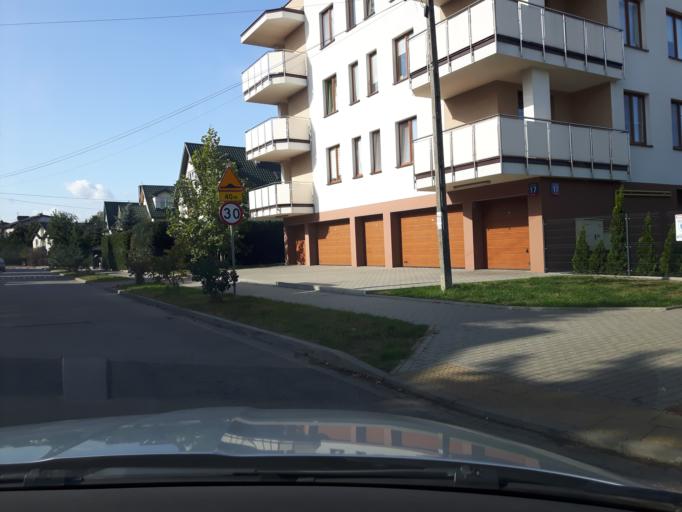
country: PL
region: Masovian Voivodeship
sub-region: Powiat wolominski
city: Zabki
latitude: 52.2831
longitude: 21.0831
